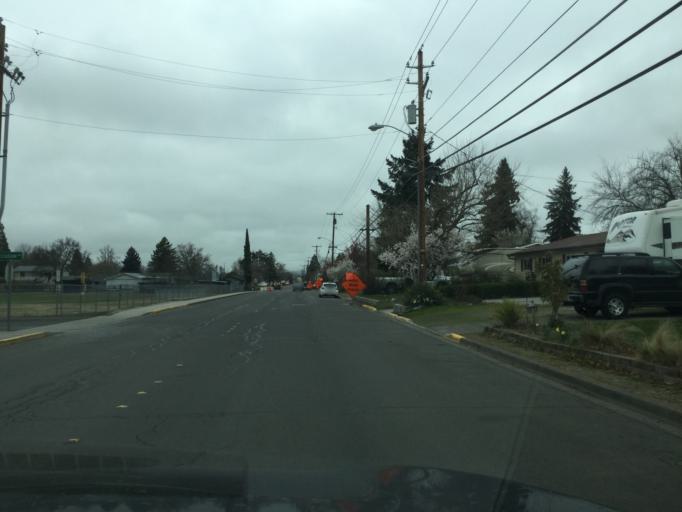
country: US
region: Oregon
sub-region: Jackson County
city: Central Point
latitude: 42.3804
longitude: -122.9196
